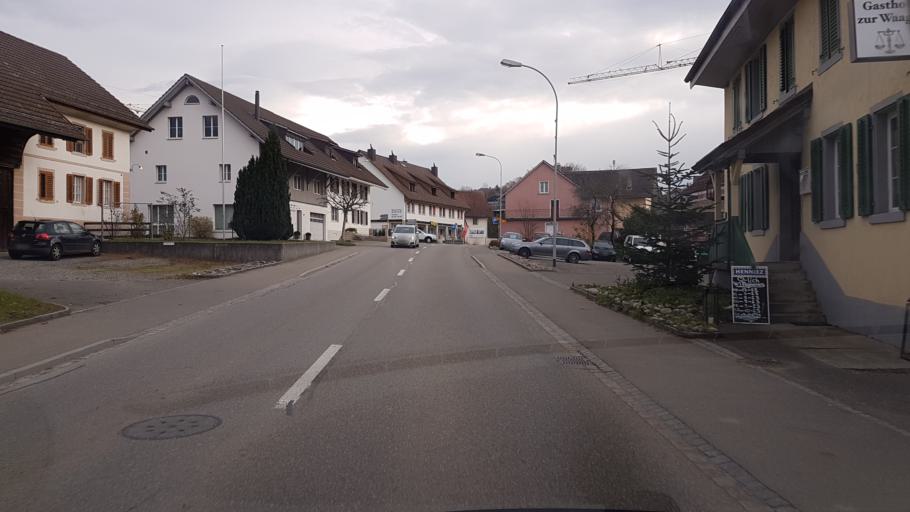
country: CH
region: Aargau
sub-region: Bezirk Baden
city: Kunten
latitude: 47.3904
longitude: 8.3296
